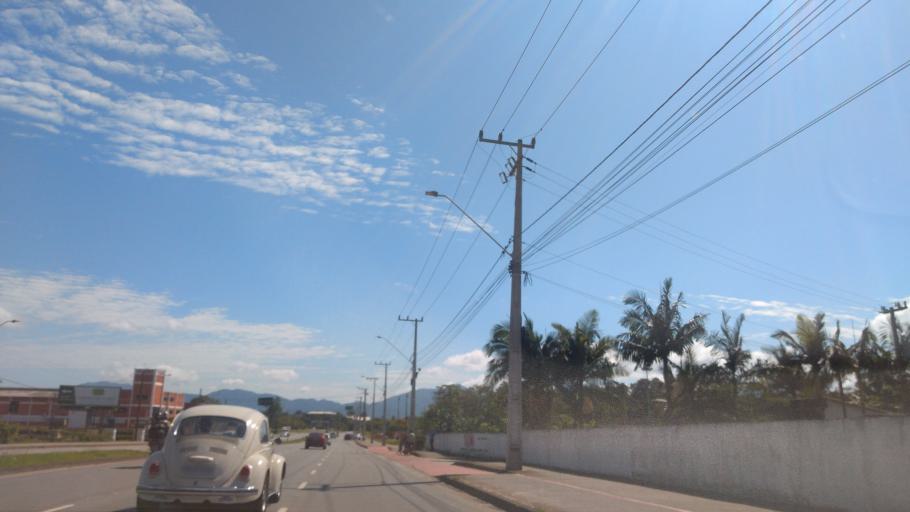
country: BR
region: Santa Catarina
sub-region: Joinville
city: Joinville
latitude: -26.2296
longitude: -48.8060
